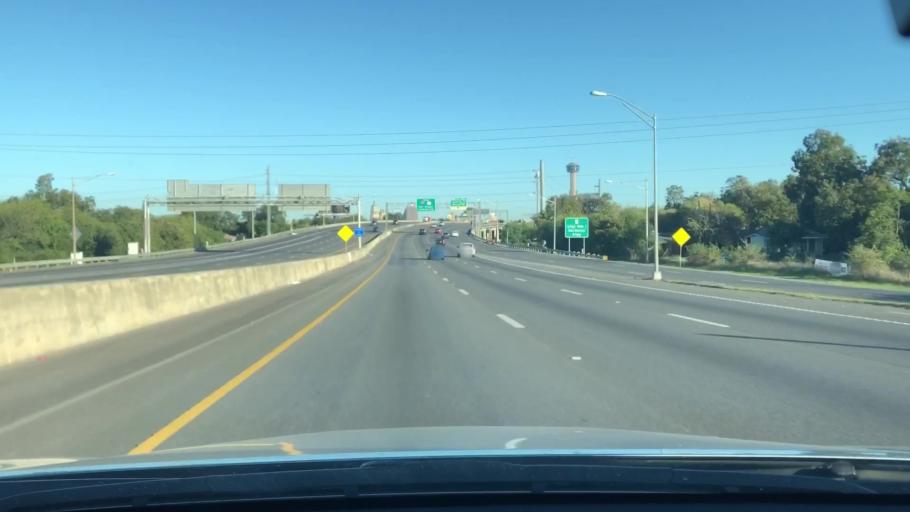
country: US
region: Texas
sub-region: Bexar County
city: San Antonio
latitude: 29.3985
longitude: -98.4796
